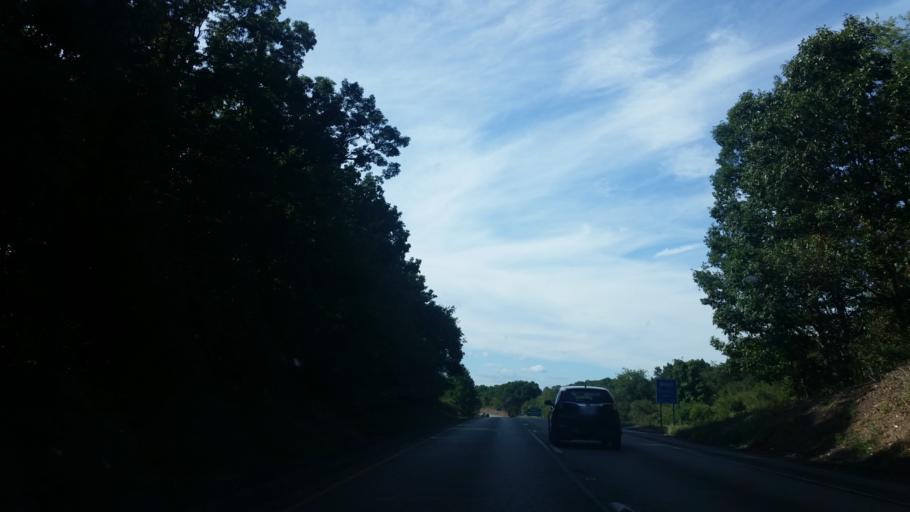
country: US
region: Pennsylvania
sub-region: Bedford County
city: Earlston
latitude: 39.9960
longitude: -78.2404
